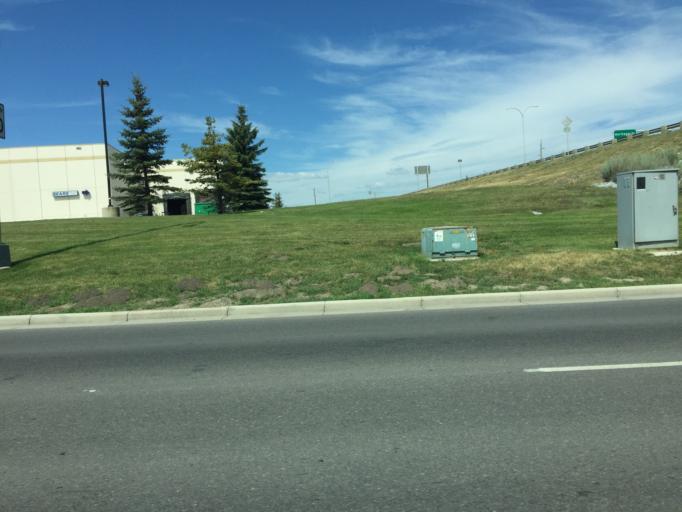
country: CA
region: Alberta
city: Calgary
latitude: 50.9871
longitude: -114.0266
